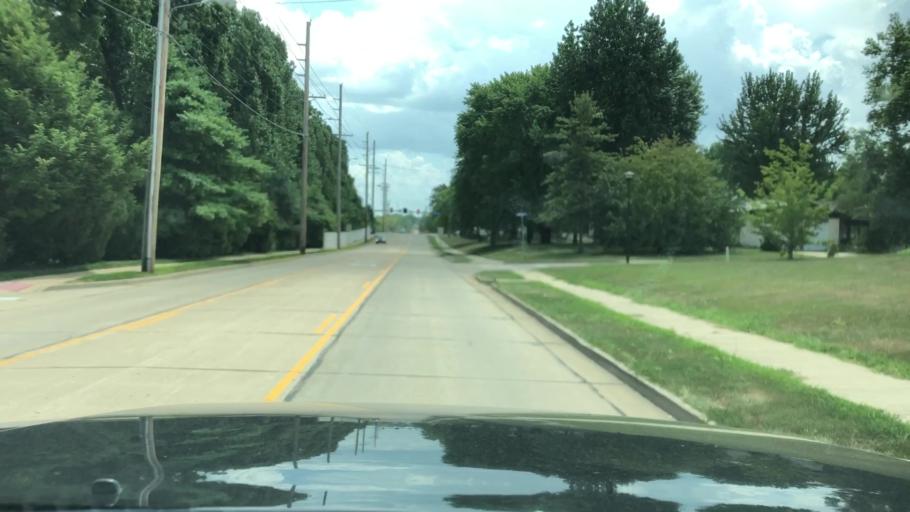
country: US
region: Missouri
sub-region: Saint Charles County
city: Saint Charles
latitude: 38.8052
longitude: -90.5355
